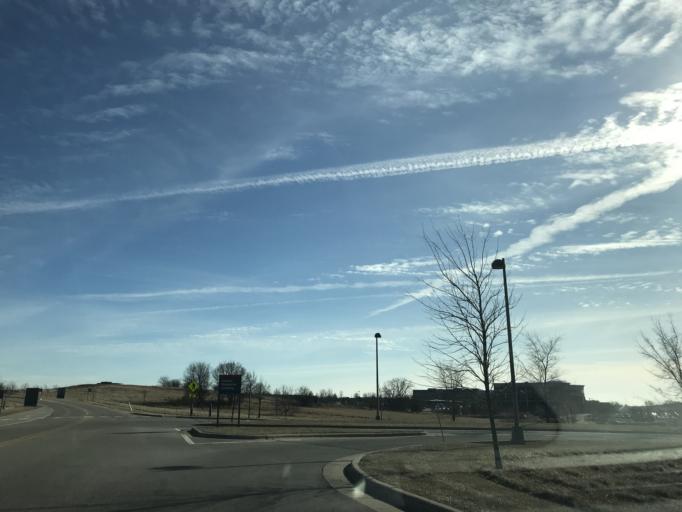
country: US
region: Wisconsin
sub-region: Dane County
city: Windsor
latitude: 43.1551
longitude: -89.2964
